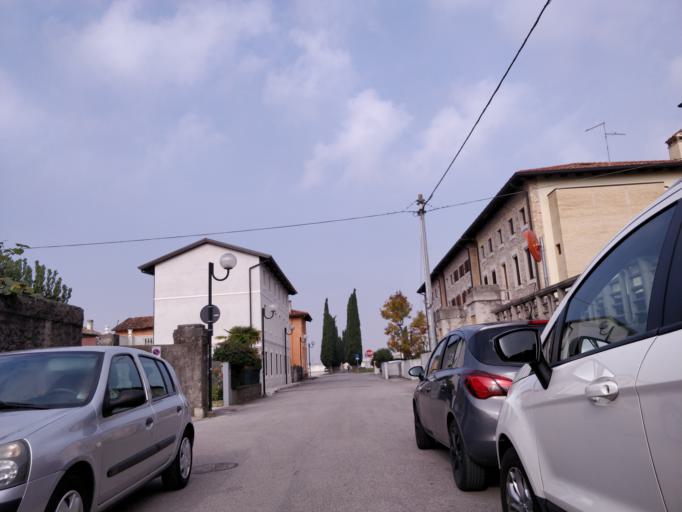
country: IT
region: Friuli Venezia Giulia
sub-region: Provincia di Udine
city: Bertiolo
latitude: 45.9431
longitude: 13.0517
